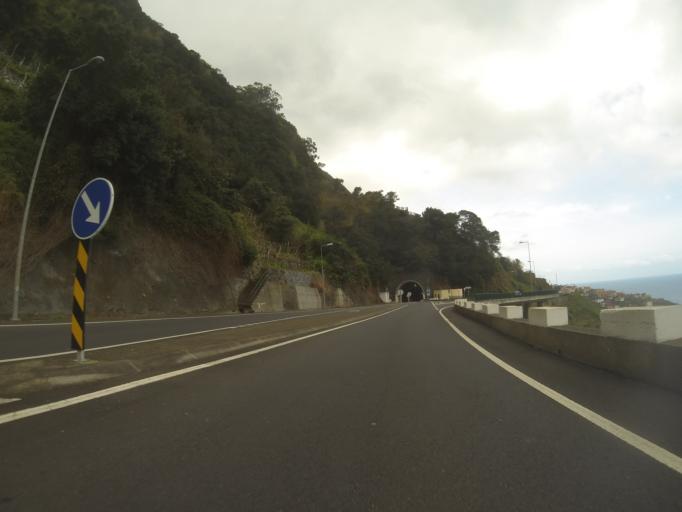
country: PT
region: Madeira
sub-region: Sao Vicente
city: Sao Vicente
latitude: 32.8195
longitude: -17.1032
